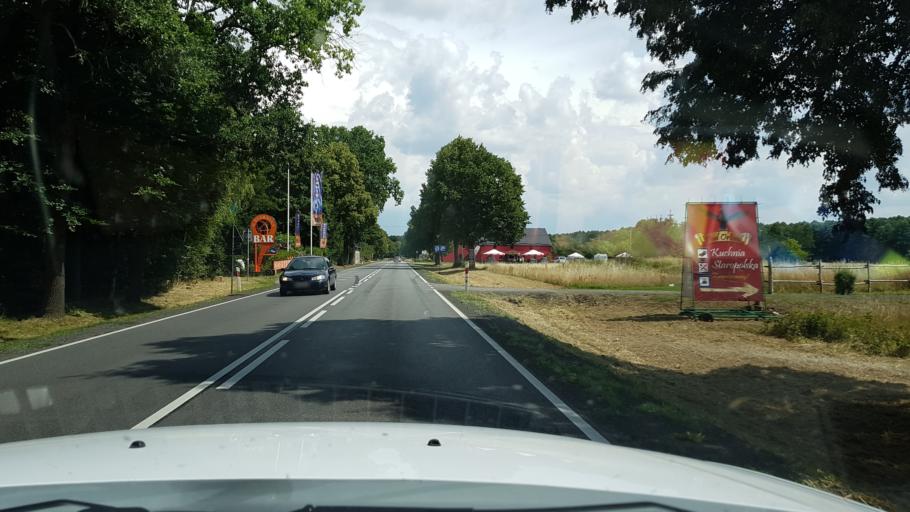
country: PL
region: West Pomeranian Voivodeship
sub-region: Powiat walecki
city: Walcz
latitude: 53.3071
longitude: 16.3955
